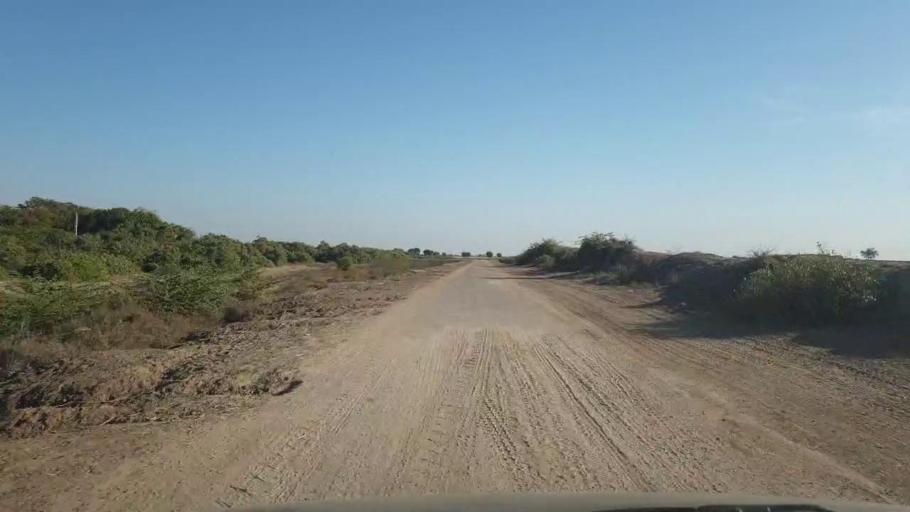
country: PK
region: Sindh
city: Dhoro Naro
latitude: 25.4272
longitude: 69.5332
